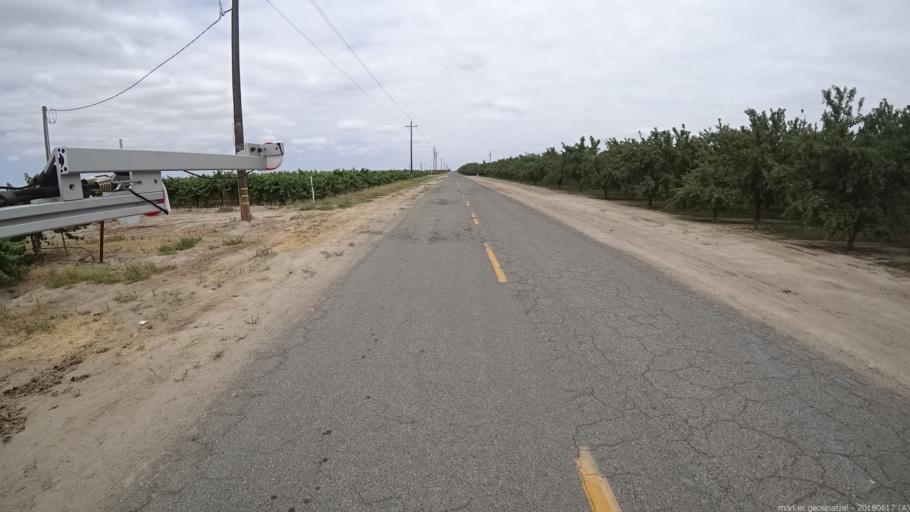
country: US
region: California
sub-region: Madera County
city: Parkwood
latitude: 36.8425
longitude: -120.1646
